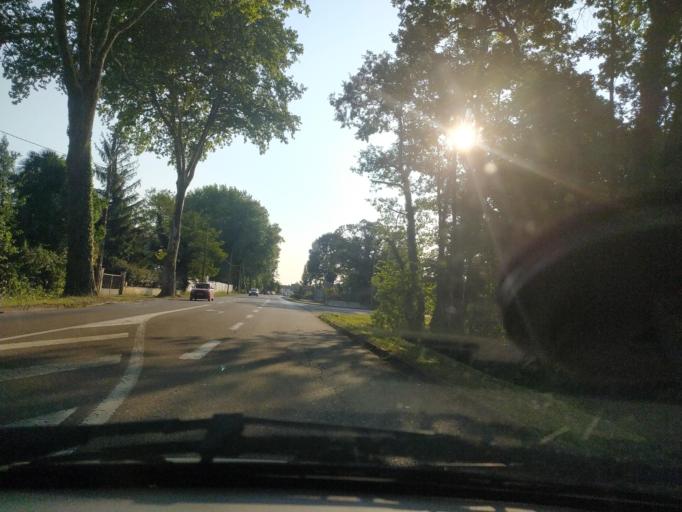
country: FR
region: Aquitaine
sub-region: Departement des Landes
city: Saint-Geours-de-Maremne
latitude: 43.6889
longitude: -1.2238
